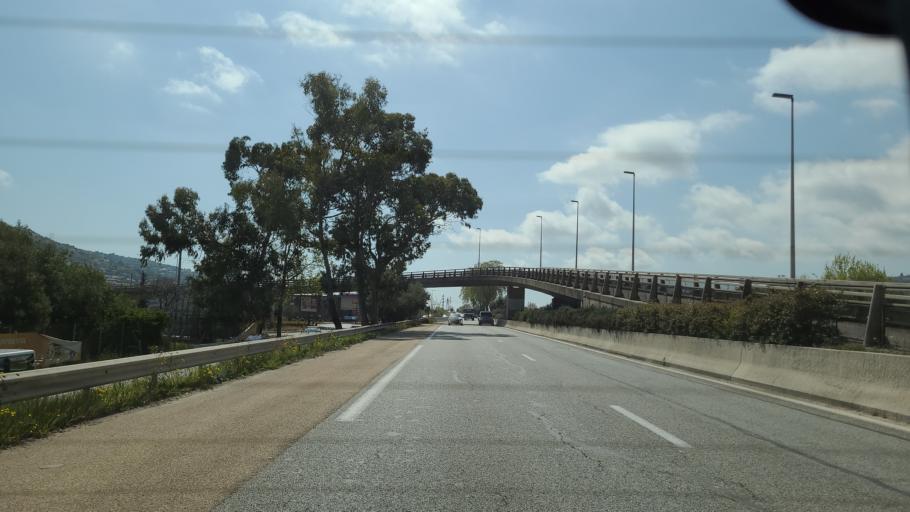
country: FR
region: Provence-Alpes-Cote d'Azur
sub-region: Departement des Alpes-Maritimes
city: Gattieres
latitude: 43.7284
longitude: 7.1853
